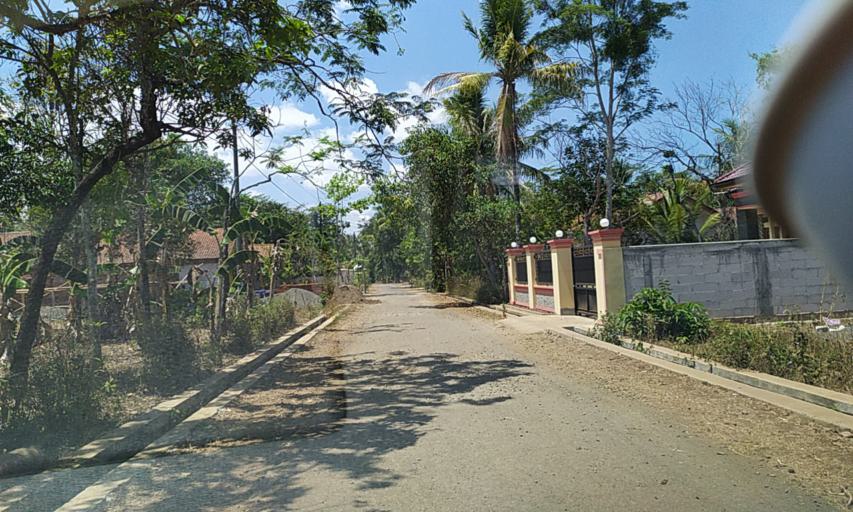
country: ID
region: Central Java
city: Kroya
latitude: -7.6498
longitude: 109.2465
